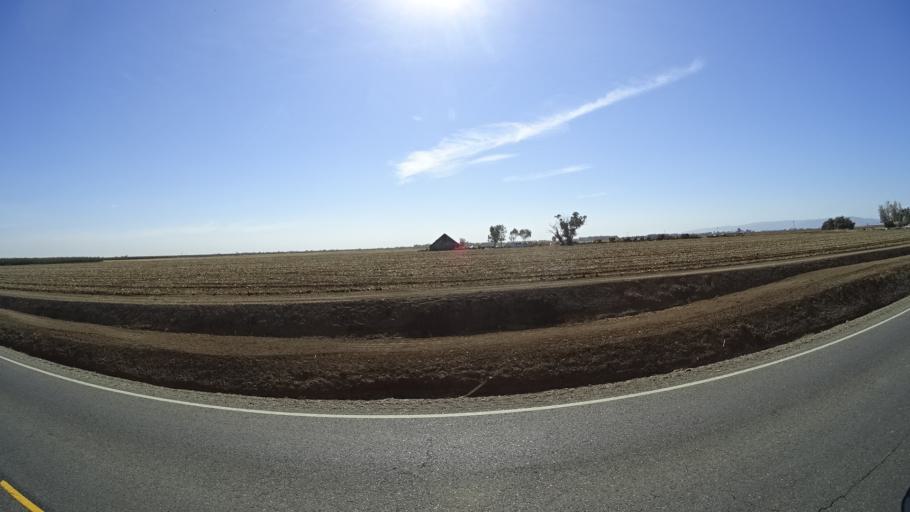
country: US
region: California
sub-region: Yolo County
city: Woodland
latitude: 38.6200
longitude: -121.8370
